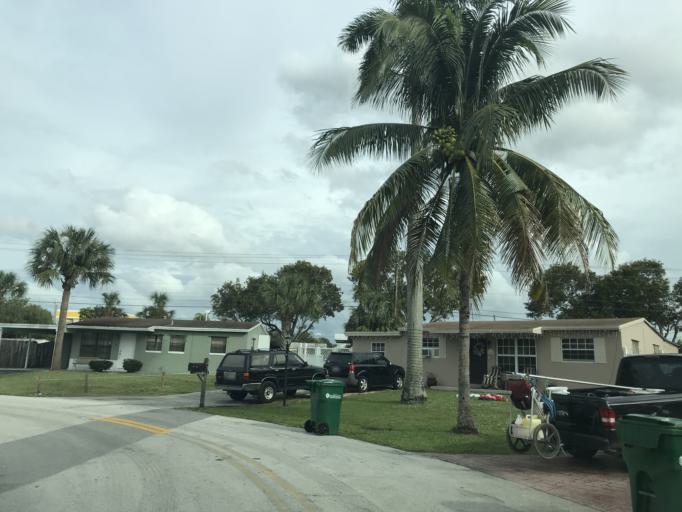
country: US
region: Florida
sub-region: Broward County
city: Margate
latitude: 26.2580
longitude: -80.2030
